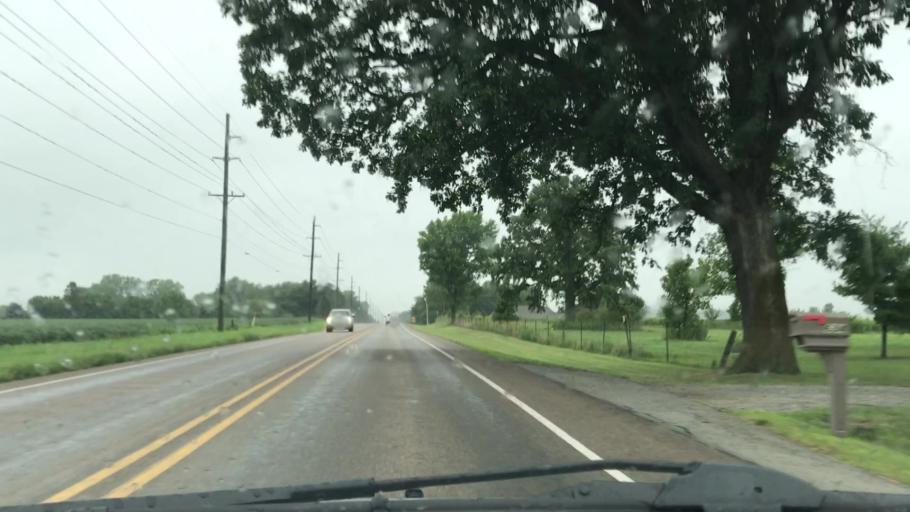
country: US
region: Indiana
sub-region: Hamilton County
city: Westfield
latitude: 40.1035
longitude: -86.1493
